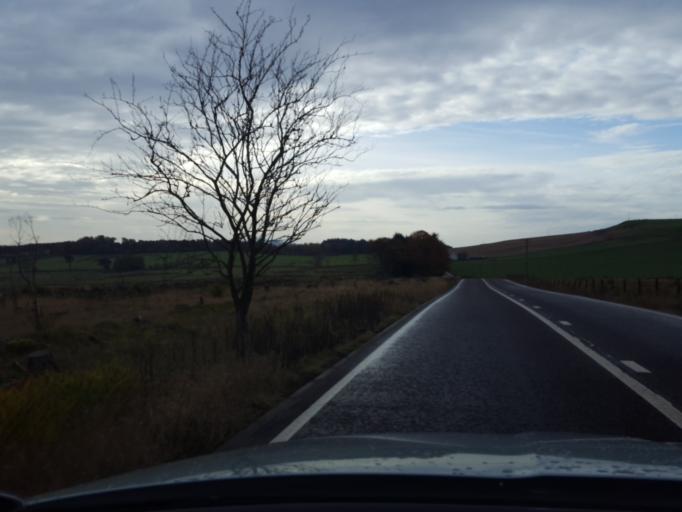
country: GB
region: Scotland
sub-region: South Lanarkshire
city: Carnwath
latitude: 55.7255
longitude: -3.5777
